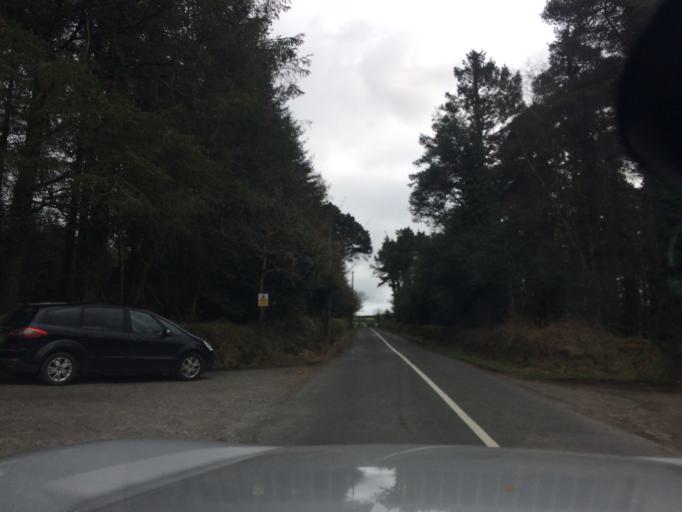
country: IE
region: Munster
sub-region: South Tipperary
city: Cluain Meala
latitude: 52.3424
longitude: -7.6330
